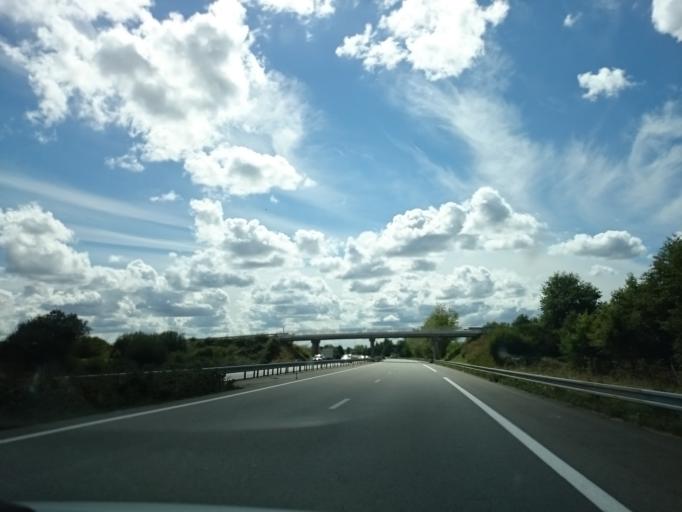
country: FR
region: Pays de la Loire
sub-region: Departement de la Loire-Atlantique
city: Saint-Mars-du-Desert
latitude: 47.3345
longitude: -1.3942
